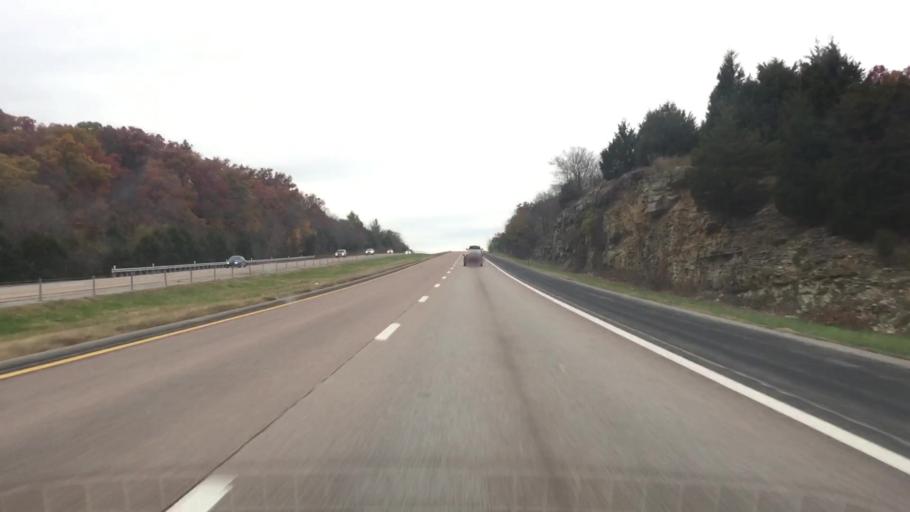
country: US
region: Missouri
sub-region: Boone County
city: Ashland
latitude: 38.6893
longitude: -92.2550
